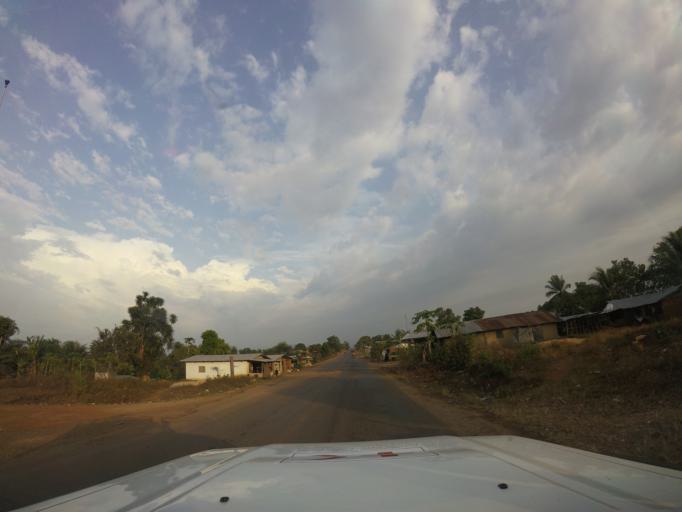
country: LR
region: Bomi
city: Tubmanburg
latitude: 6.7184
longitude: -10.9765
